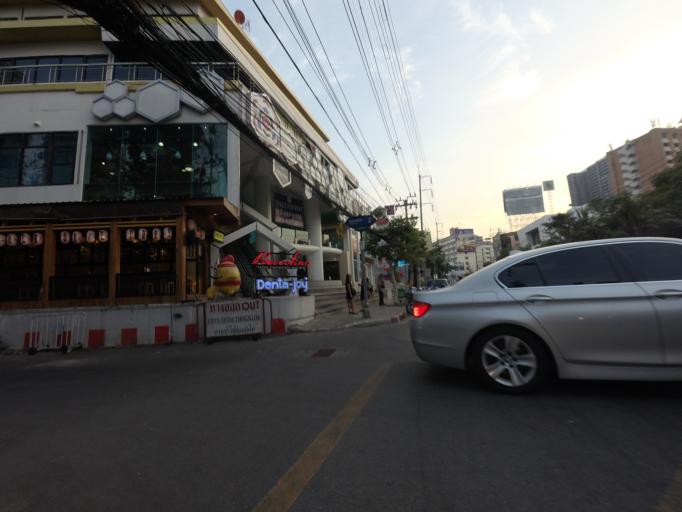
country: TH
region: Bangkok
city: Watthana
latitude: 13.7264
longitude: 100.5801
